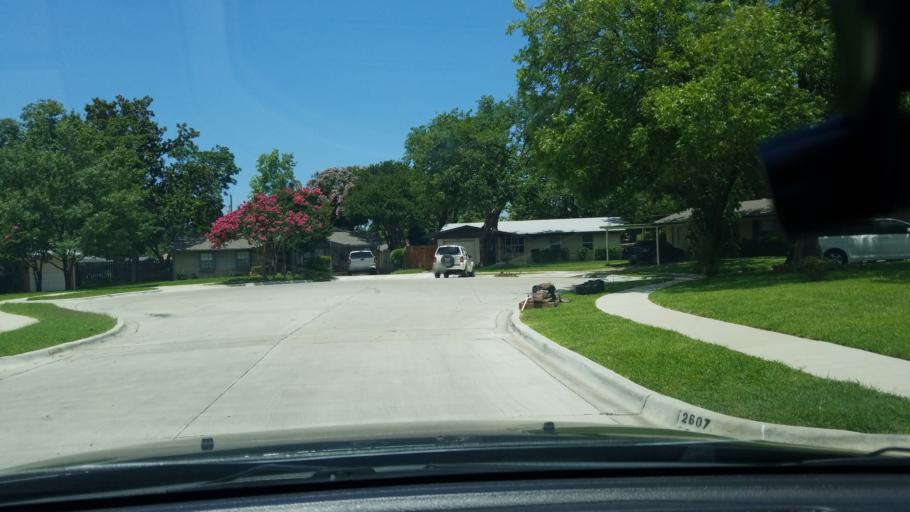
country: US
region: Texas
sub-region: Dallas County
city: Mesquite
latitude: 32.8005
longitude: -96.6529
